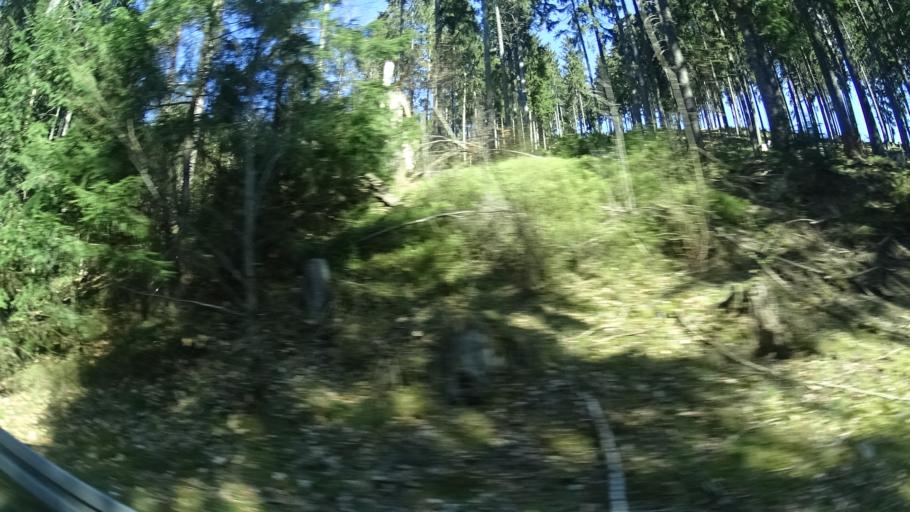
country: DE
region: Thuringia
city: Wildenspring
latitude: 50.5793
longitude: 11.0670
